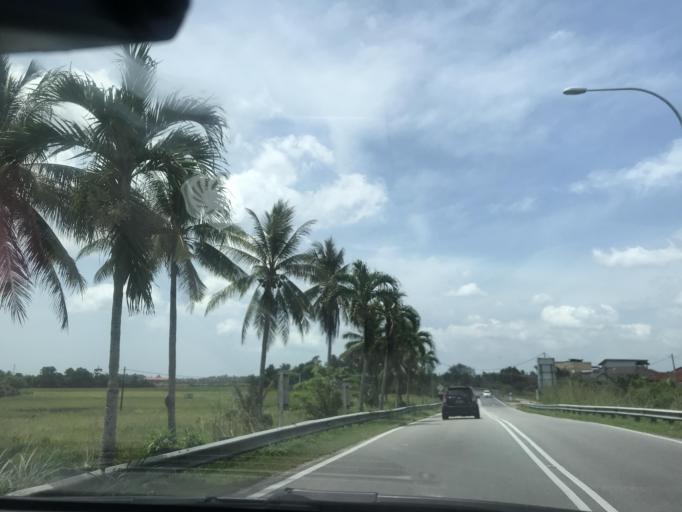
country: MY
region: Kelantan
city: Kota Bharu
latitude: 6.1532
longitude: 102.2057
